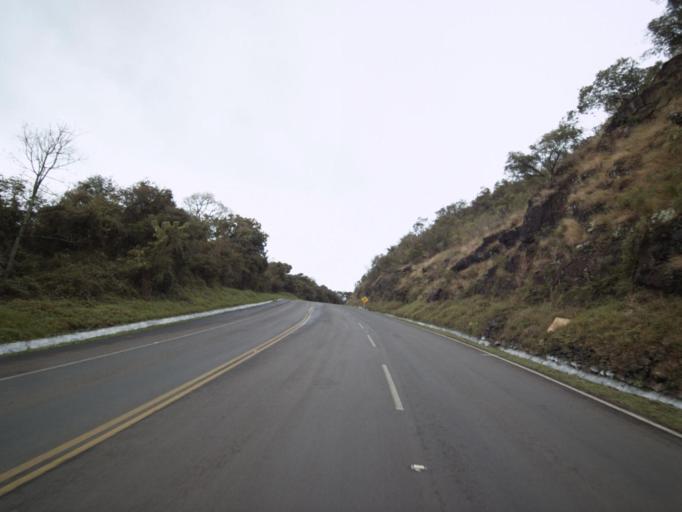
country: BR
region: Santa Catarina
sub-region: Concordia
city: Concordia
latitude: -27.0578
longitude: -51.8903
